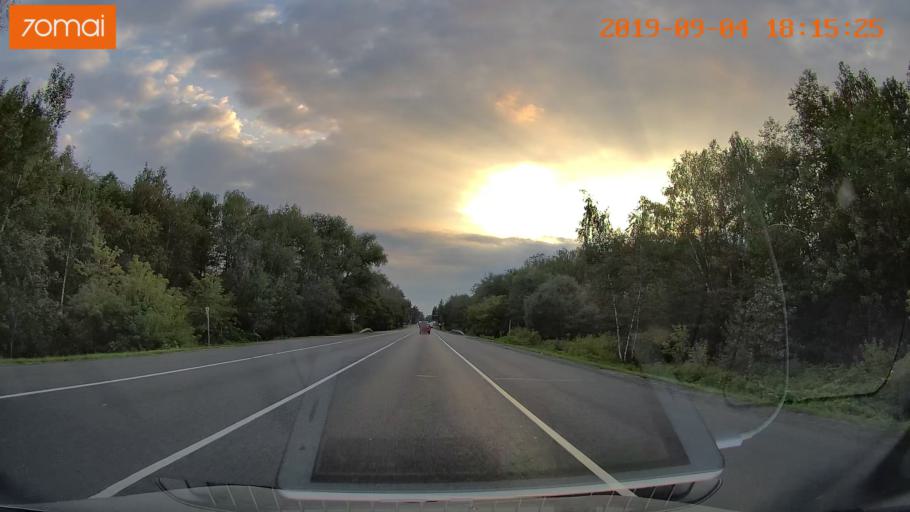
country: RU
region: Moskovskaya
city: Lopatinskiy
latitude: 55.3471
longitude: 38.7030
